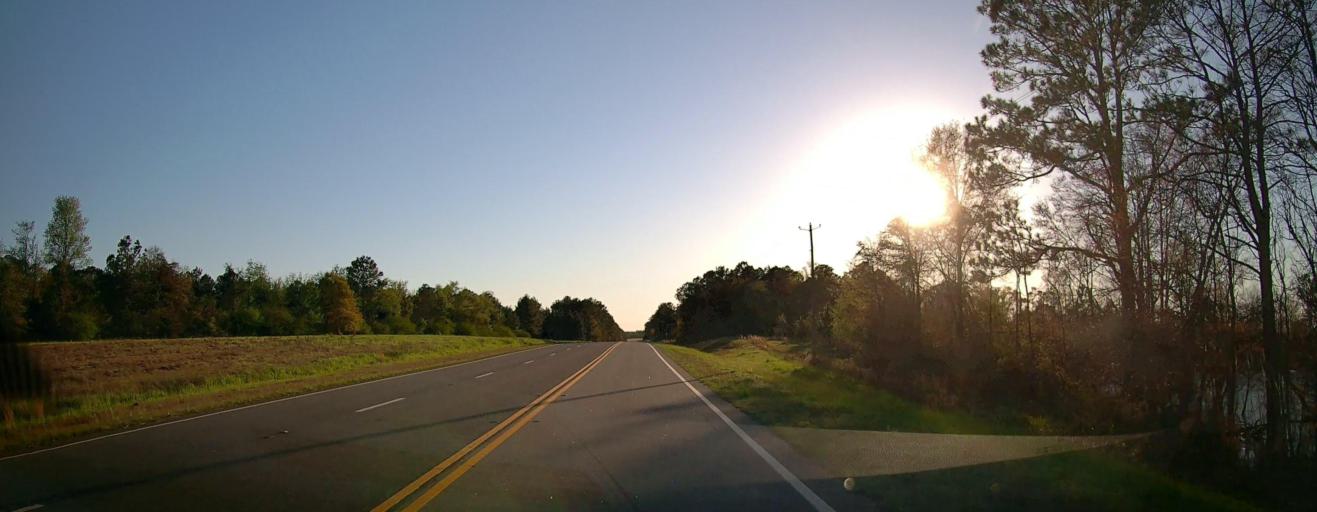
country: US
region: Georgia
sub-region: Wilcox County
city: Abbeville
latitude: 31.9793
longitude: -83.3558
